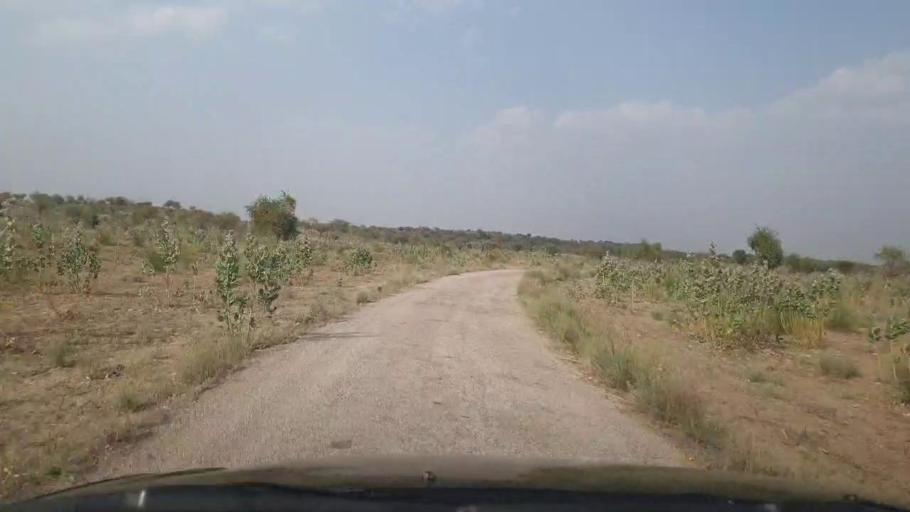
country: PK
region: Sindh
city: Islamkot
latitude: 25.0380
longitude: 70.5622
